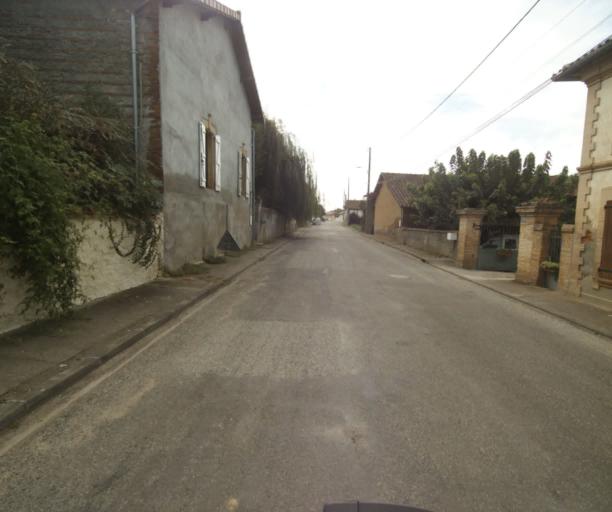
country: FR
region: Midi-Pyrenees
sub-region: Departement du Tarn-et-Garonne
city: Finhan
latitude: 43.9095
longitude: 1.2194
